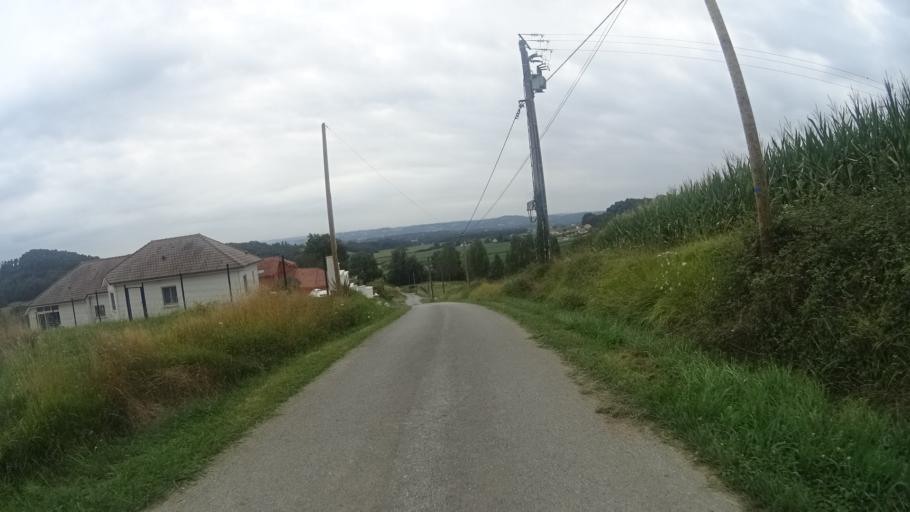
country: FR
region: Aquitaine
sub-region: Departement des Pyrenees-Atlantiques
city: Mont
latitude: 43.4937
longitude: -0.6926
